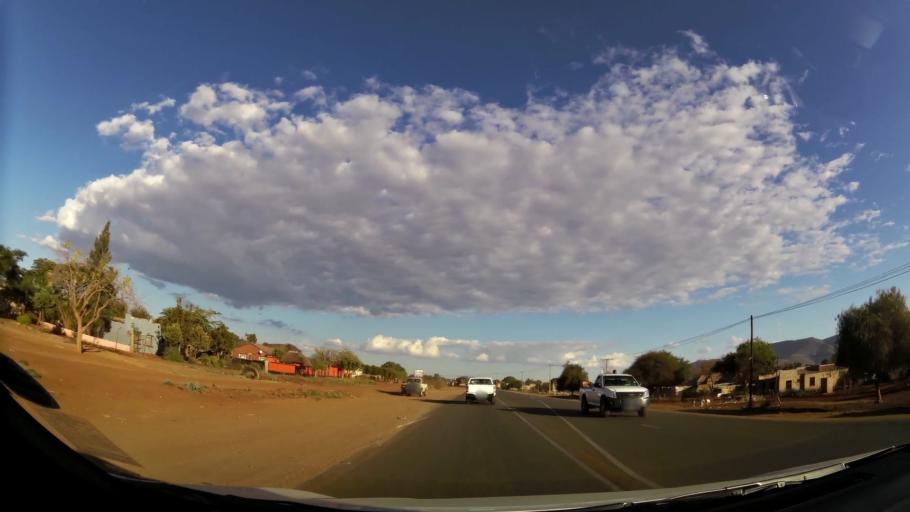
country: ZA
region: Limpopo
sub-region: Waterberg District Municipality
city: Mokopane
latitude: -24.1687
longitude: 28.9848
